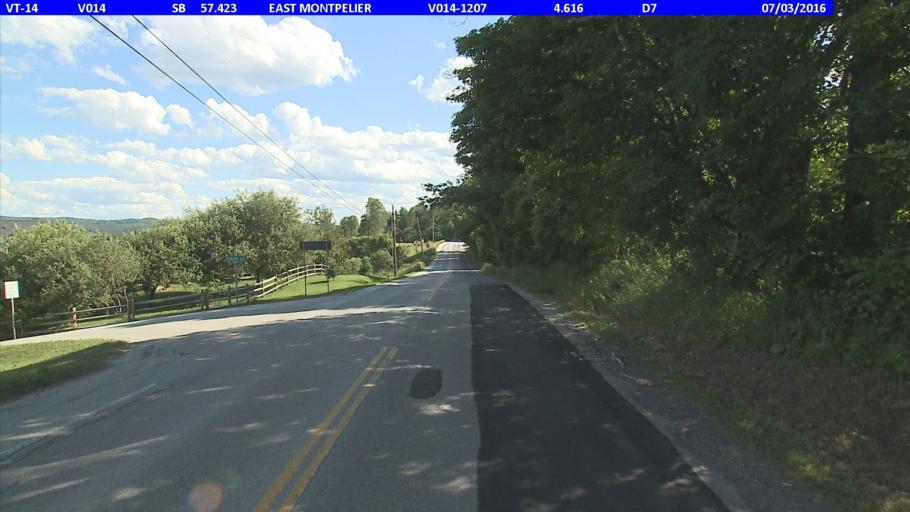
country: US
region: Vermont
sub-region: Washington County
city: Barre
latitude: 44.2934
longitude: -72.4575
